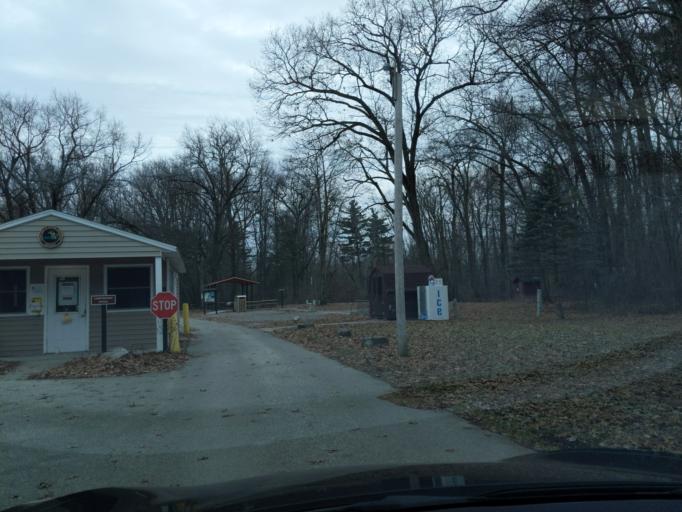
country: US
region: Michigan
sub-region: Bay County
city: Bay City
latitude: 43.6660
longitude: -83.9058
